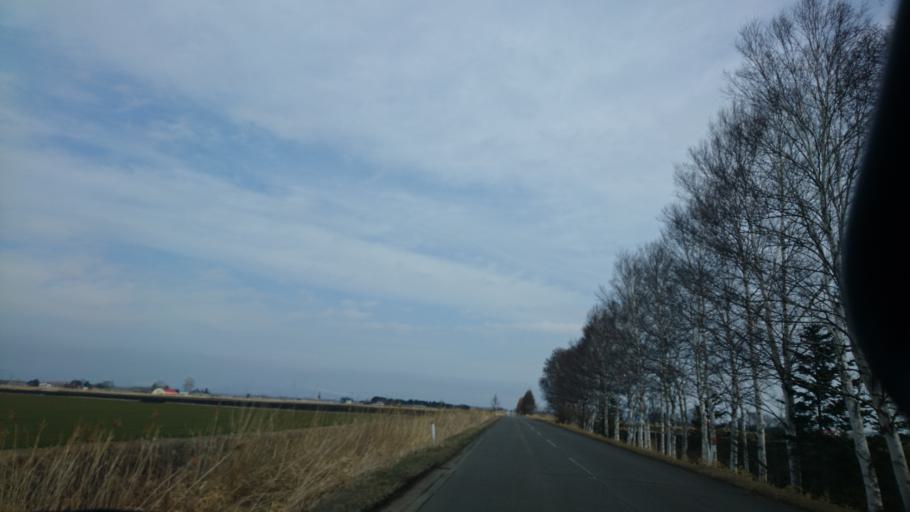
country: JP
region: Hokkaido
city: Otofuke
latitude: 43.0467
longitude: 143.2323
